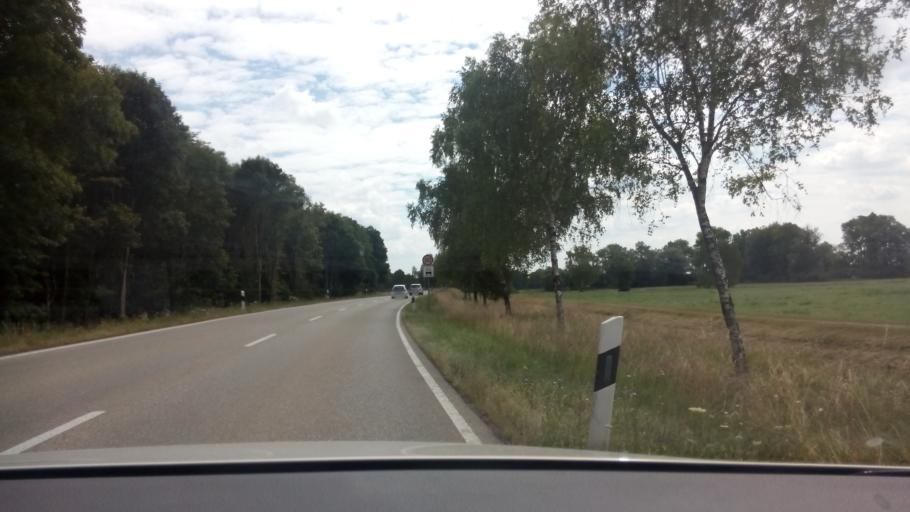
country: DE
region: Bavaria
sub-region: Upper Bavaria
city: Marzling
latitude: 48.3748
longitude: 11.8112
